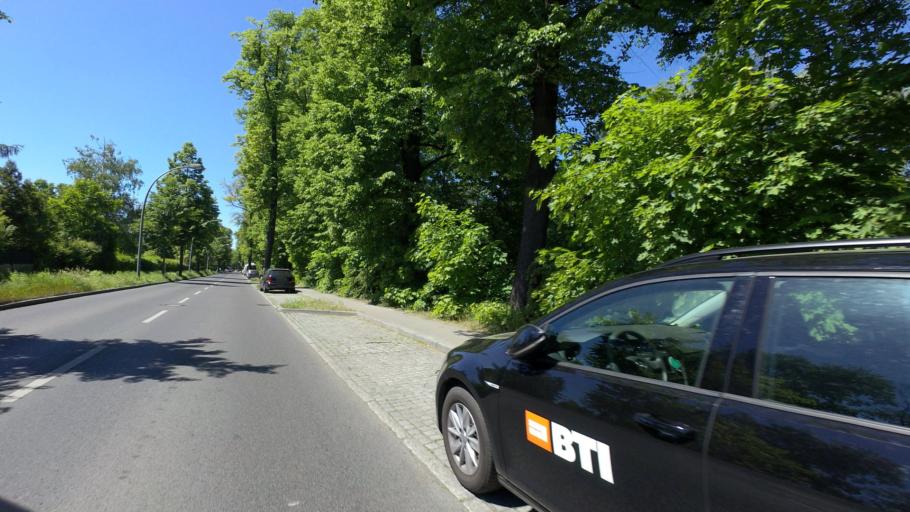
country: DE
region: Berlin
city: Siemensstadt
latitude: 52.5477
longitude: 13.2523
